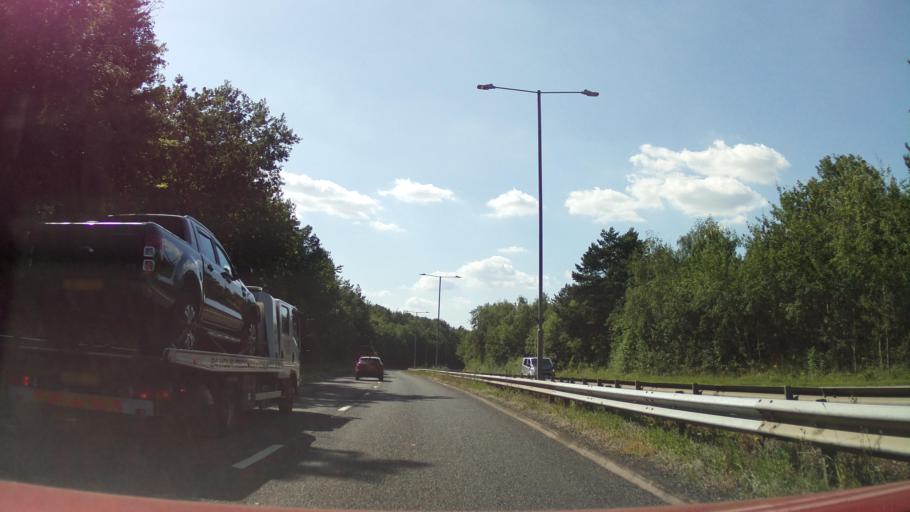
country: GB
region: England
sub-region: Worcestershire
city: Redditch
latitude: 52.3023
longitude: -1.9688
